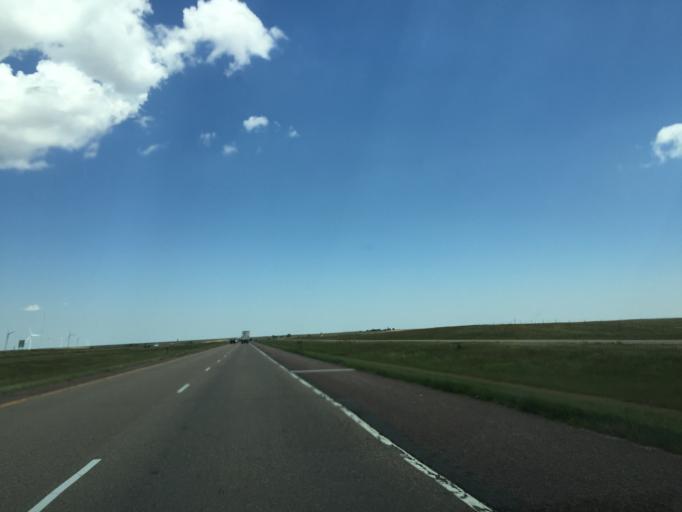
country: US
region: Colorado
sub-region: Lincoln County
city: Hugo
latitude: 39.2787
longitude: -103.4149
